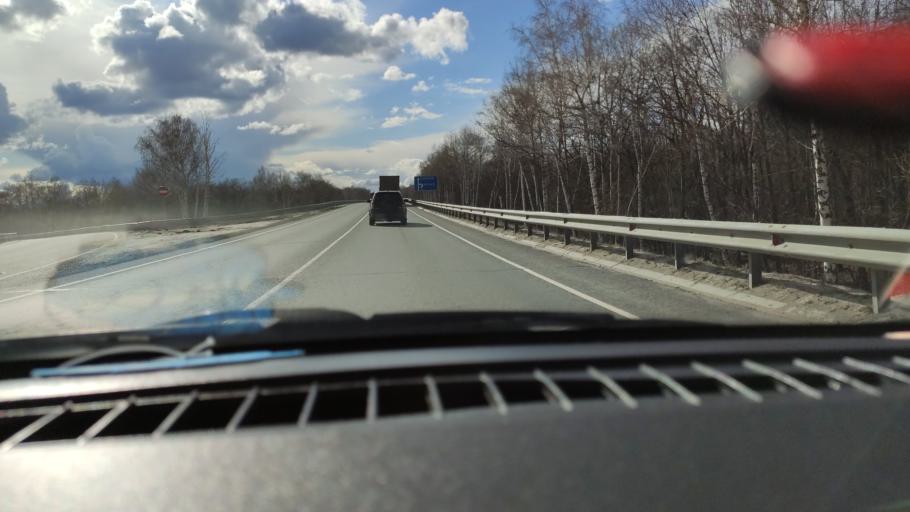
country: RU
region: Saratov
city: Vol'sk
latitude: 52.1091
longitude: 47.3784
